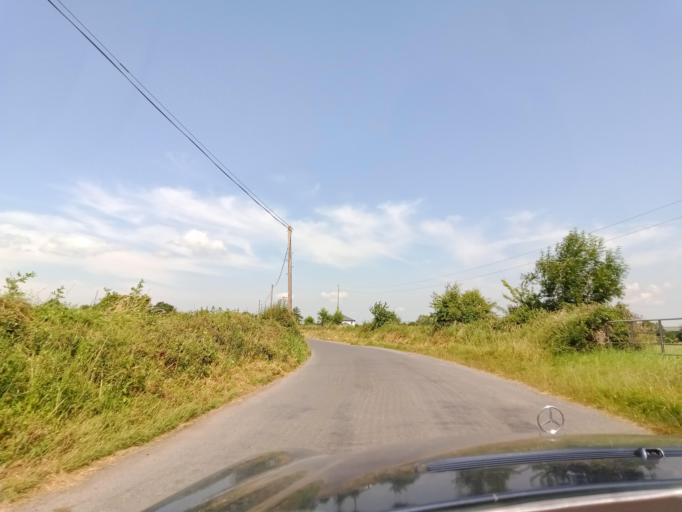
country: IE
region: Leinster
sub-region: Kilkenny
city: Mooncoin
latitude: 52.2815
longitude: -7.2383
